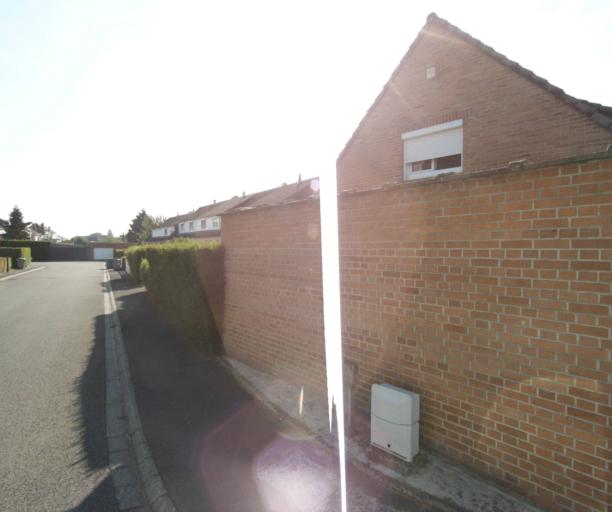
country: FR
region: Nord-Pas-de-Calais
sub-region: Departement du Nord
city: Mouvaux
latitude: 50.7126
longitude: 3.1302
